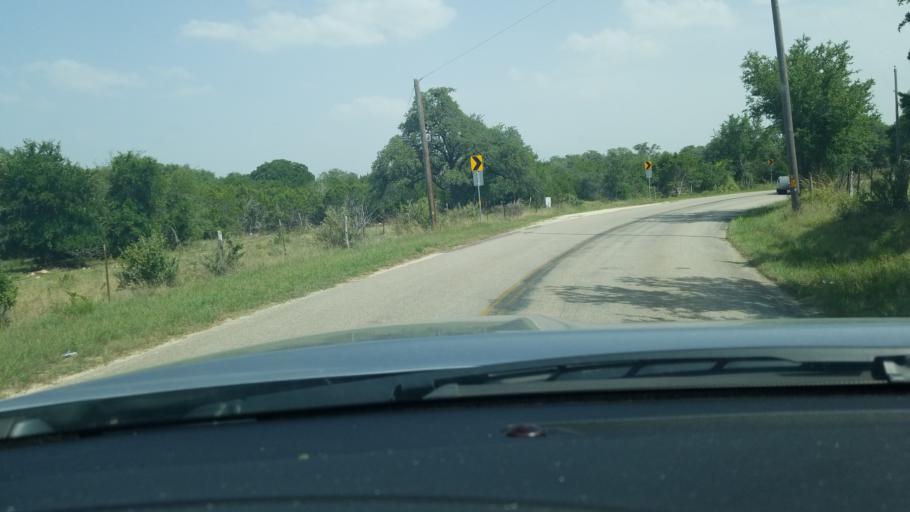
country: US
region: Texas
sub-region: Comal County
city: Bulverde
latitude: 29.7504
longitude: -98.4577
